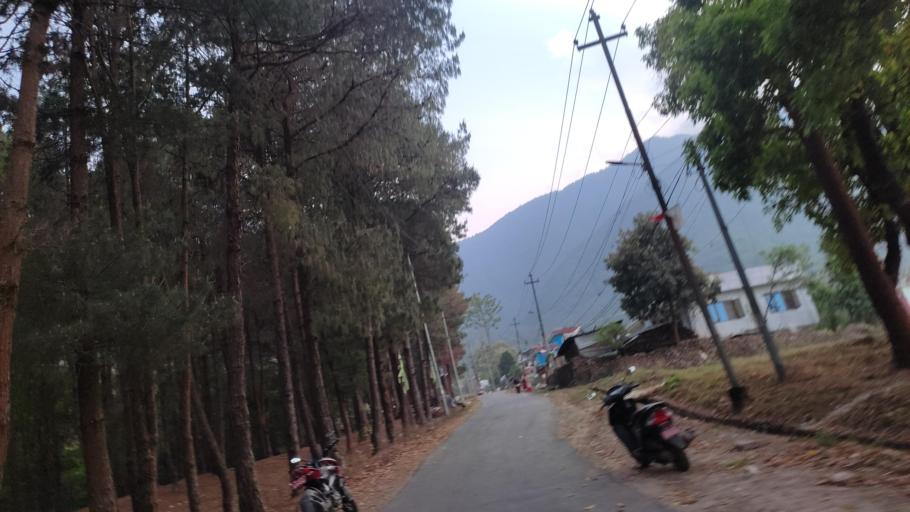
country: NP
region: Central Region
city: Kirtipur
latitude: 27.6612
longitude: 85.2533
